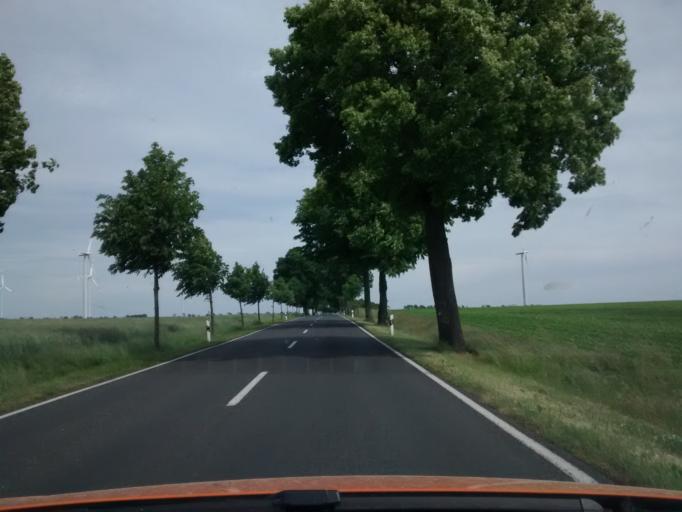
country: DE
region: Brandenburg
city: Ihlow
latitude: 51.8896
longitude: 13.3103
